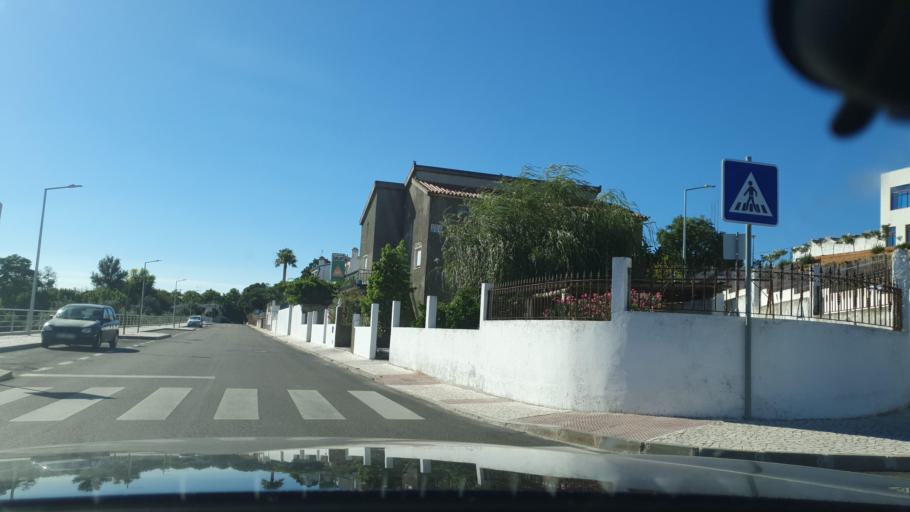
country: PT
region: Evora
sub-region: Alandroal
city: Alandroal
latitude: 38.7043
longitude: -7.4041
